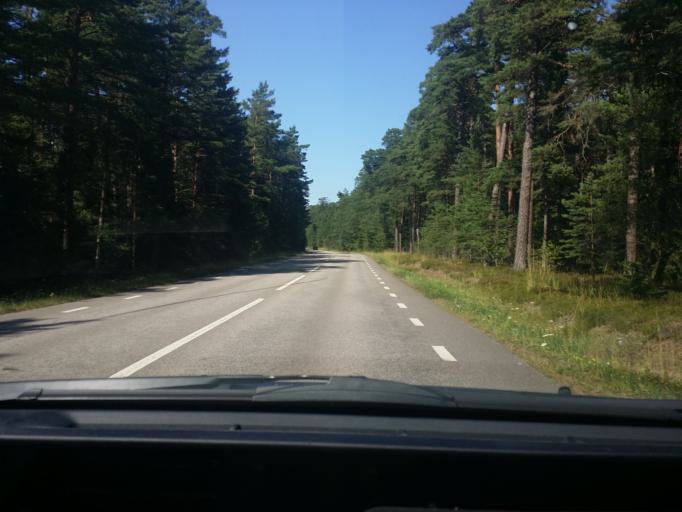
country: SE
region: Kalmar
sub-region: Borgholms Kommun
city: Borgholm
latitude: 57.2685
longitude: 17.0267
